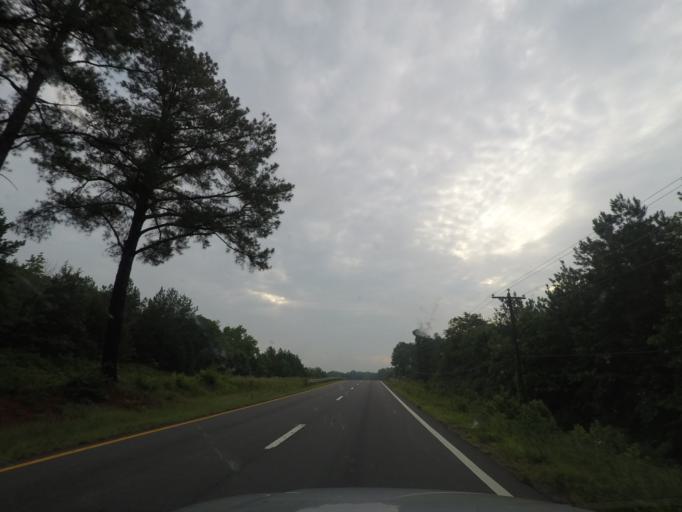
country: US
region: Virginia
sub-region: Halifax County
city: Halifax
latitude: 36.8054
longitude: -78.7638
